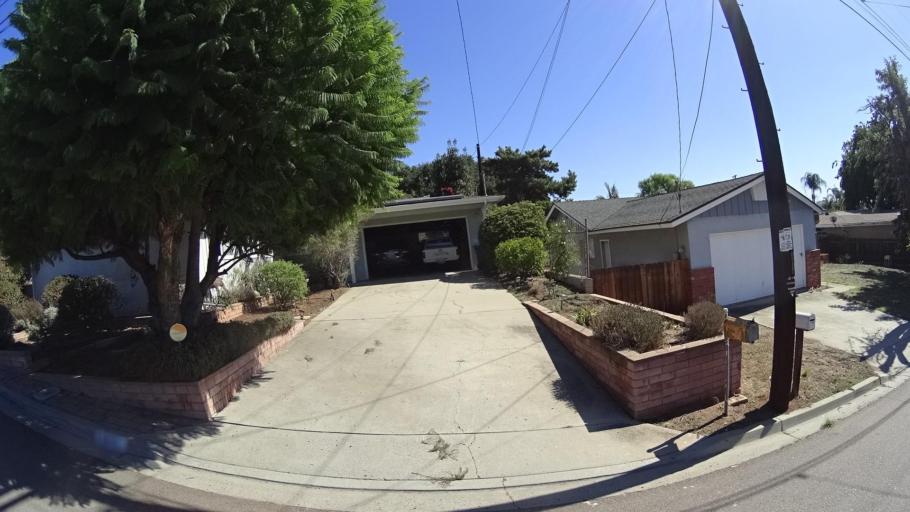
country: US
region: California
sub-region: San Diego County
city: Santee
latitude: 32.8283
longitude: -116.9556
